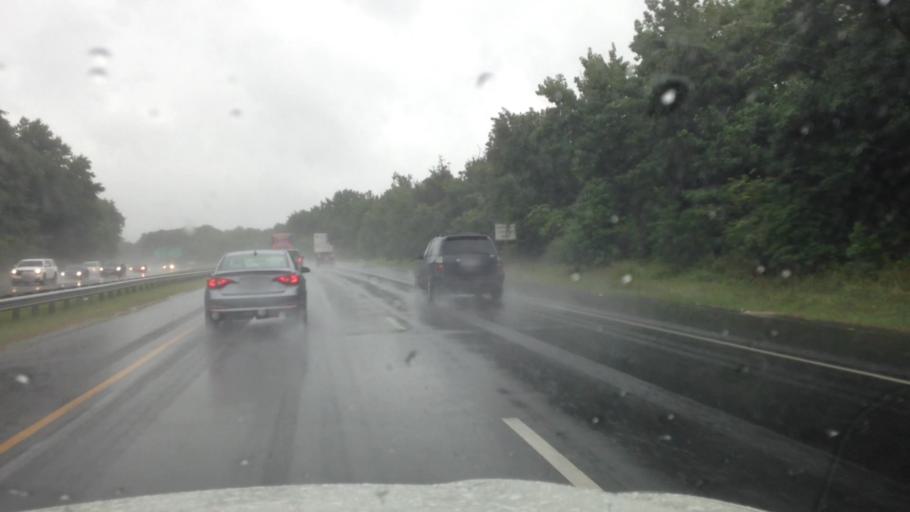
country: US
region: Maryland
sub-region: Prince George's County
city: Cheverly
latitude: 38.9210
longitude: -76.9072
